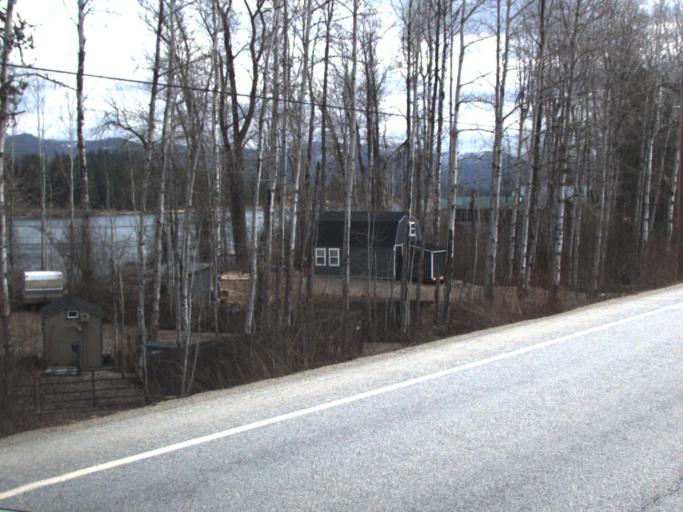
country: US
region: Washington
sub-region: Pend Oreille County
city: Newport
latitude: 48.2330
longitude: -117.2164
